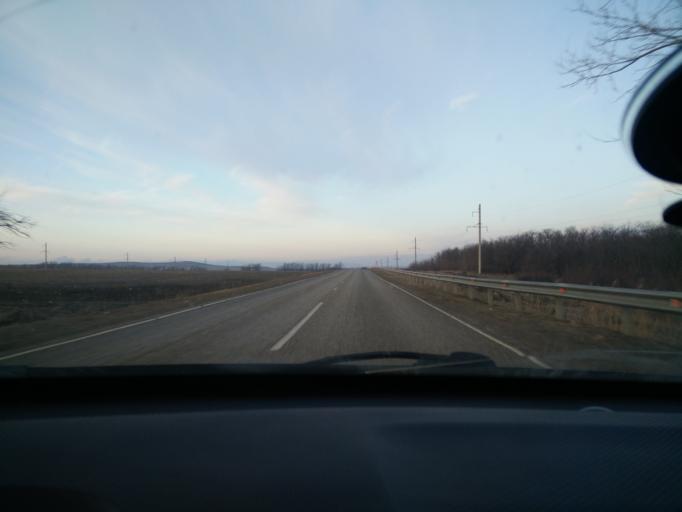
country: RU
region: Stavropol'skiy
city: Tatarka
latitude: 44.9965
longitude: 41.7475
